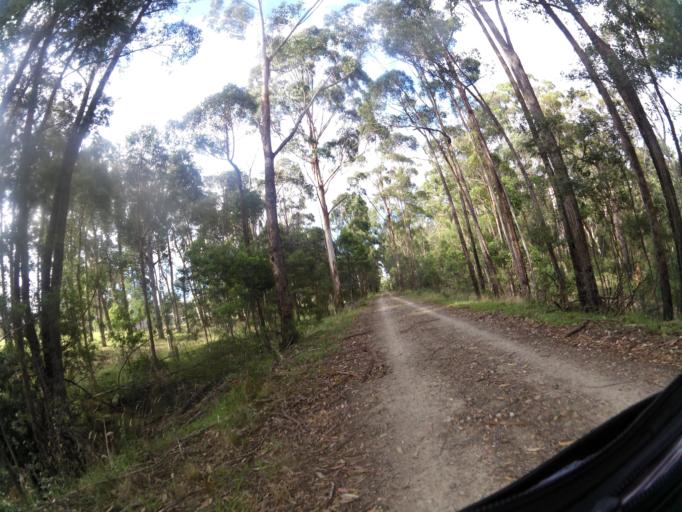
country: AU
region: Victoria
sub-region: East Gippsland
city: Lakes Entrance
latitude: -37.7383
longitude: 148.4204
